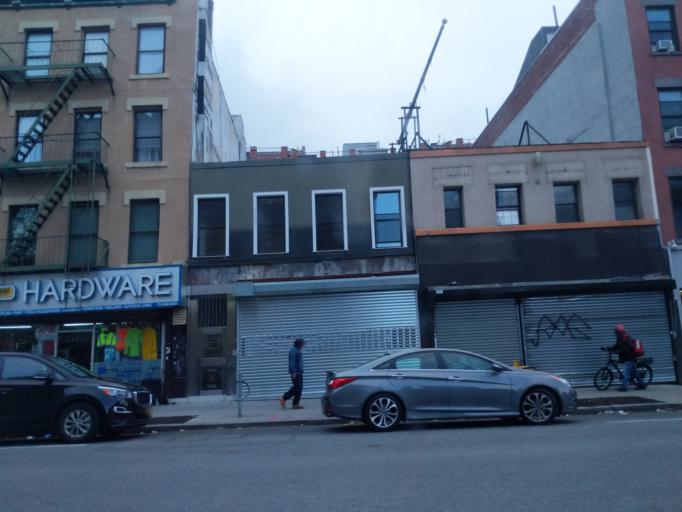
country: US
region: New York
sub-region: New York County
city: Manhattan
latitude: 40.7900
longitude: -73.9458
